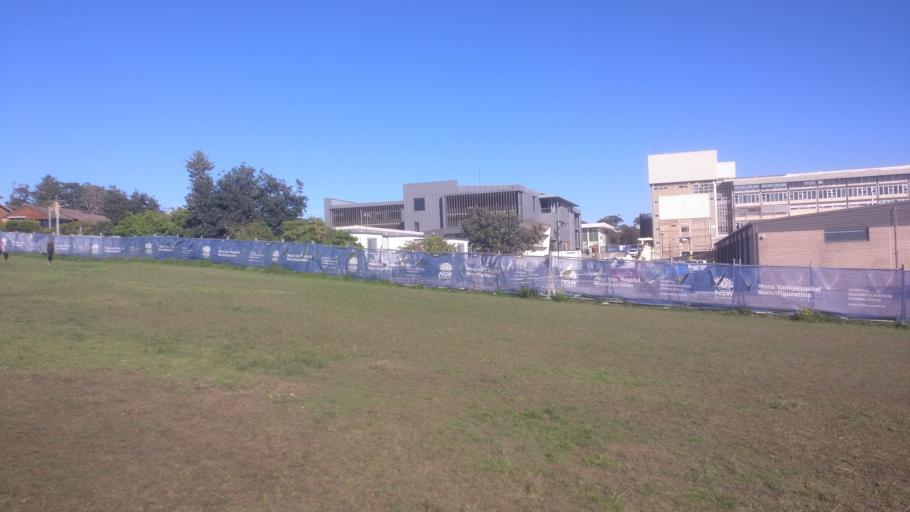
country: AU
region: New South Wales
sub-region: Pittwater
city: Warriewood
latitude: -33.6851
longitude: 151.3088
